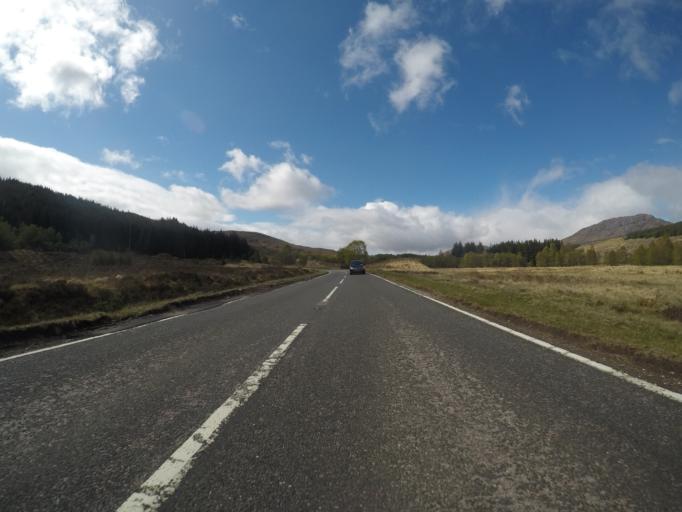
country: GB
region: Scotland
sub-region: Highland
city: Spean Bridge
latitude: 57.1307
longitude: -4.9610
